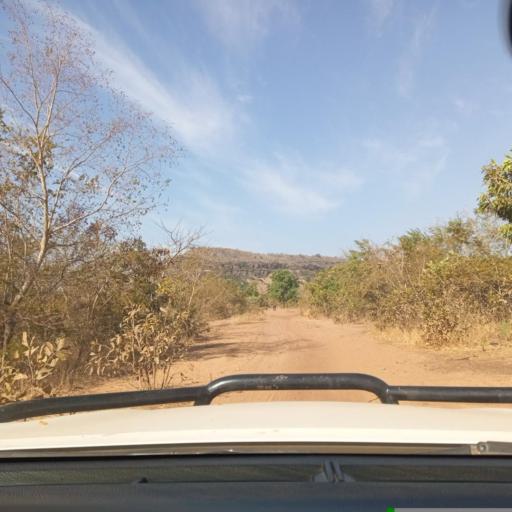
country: ML
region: Bamako
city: Bamako
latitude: 12.5560
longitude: -8.1451
